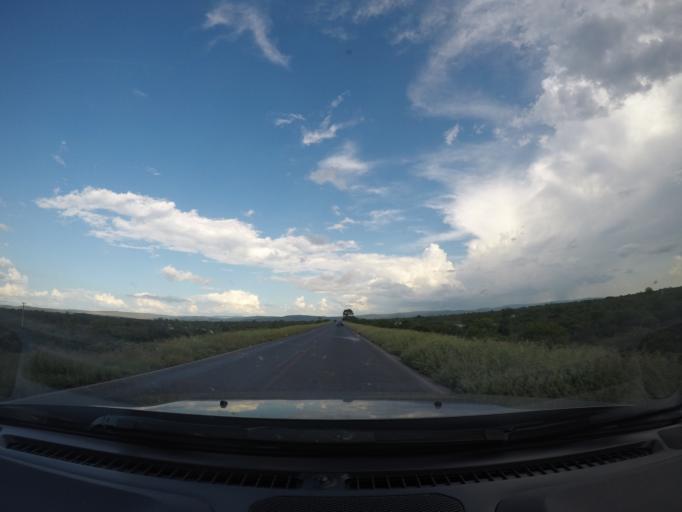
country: BR
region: Bahia
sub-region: Ibotirama
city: Ibotirama
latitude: -12.1696
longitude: -43.2675
